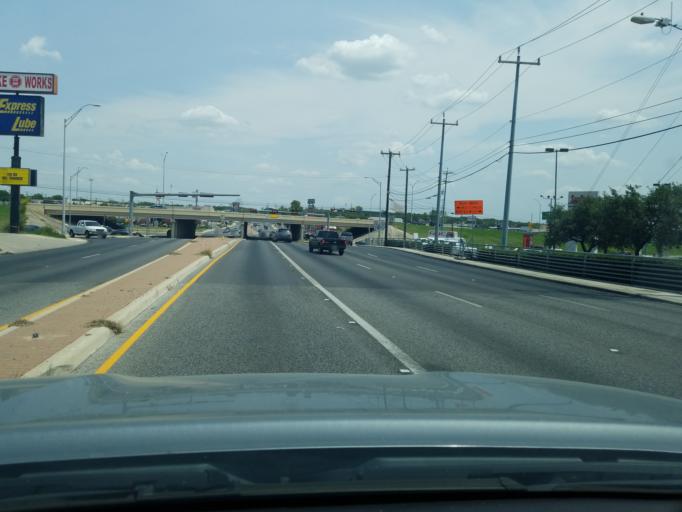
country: US
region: Texas
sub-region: Bexar County
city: Hollywood Park
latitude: 29.5657
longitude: -98.4835
